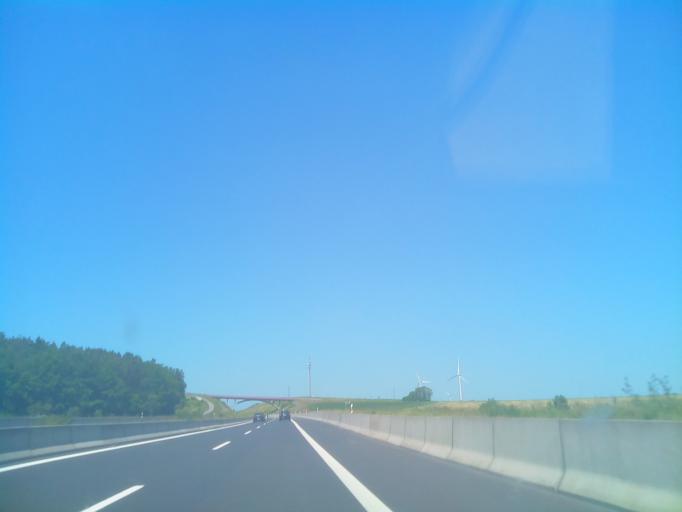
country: DE
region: Bavaria
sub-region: Regierungsbezirk Unterfranken
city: Rannungen
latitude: 50.1692
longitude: 10.1855
